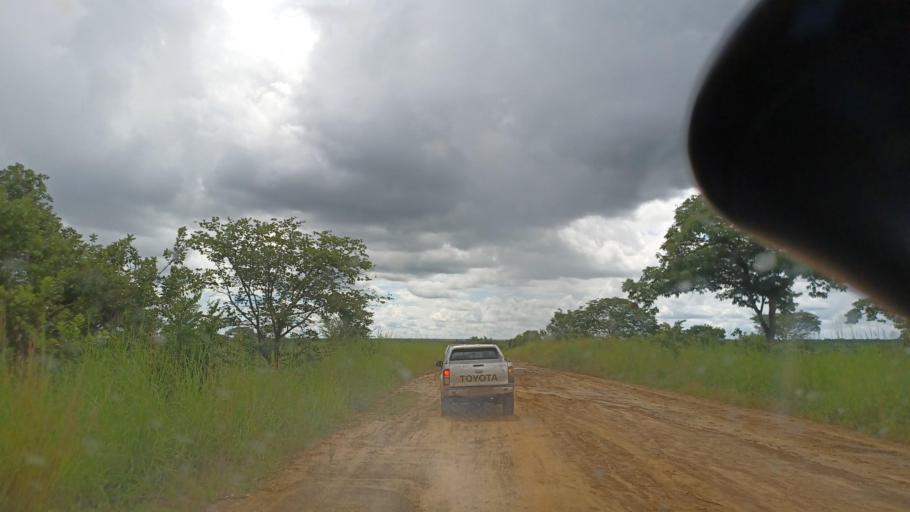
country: ZM
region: North-Western
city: Kabompo
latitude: -13.4203
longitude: 24.3984
